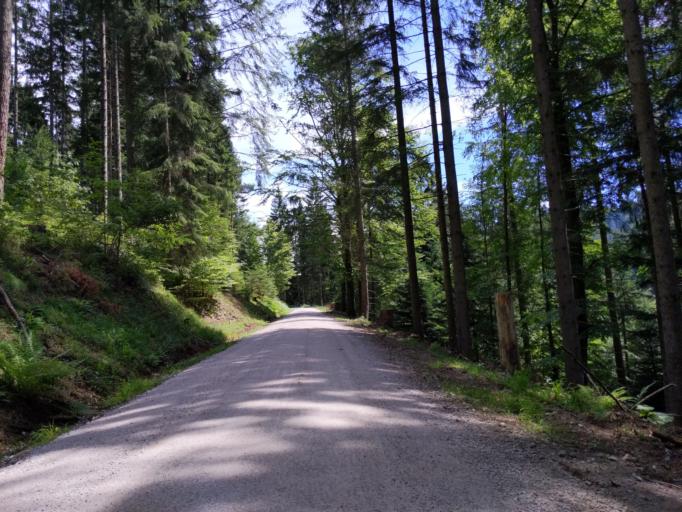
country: DE
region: Baden-Wuerttemberg
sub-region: Karlsruhe Region
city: Bad Rippoldsau-Schapbach
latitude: 48.4146
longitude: 8.3633
